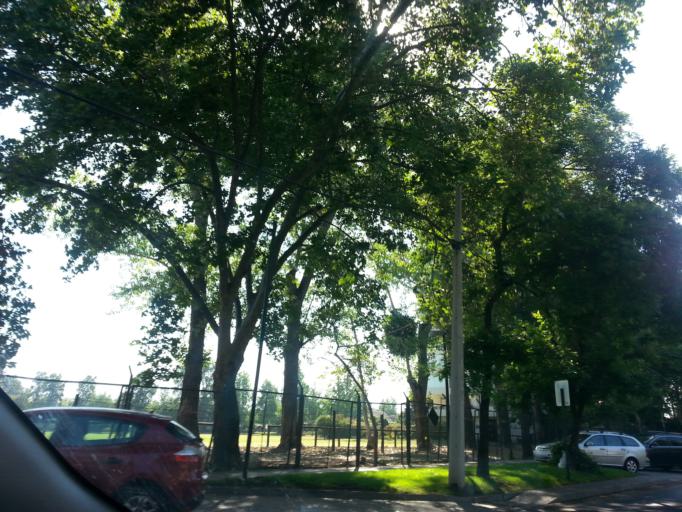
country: CL
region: Santiago Metropolitan
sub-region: Provincia de Santiago
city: Villa Presidente Frei, Nunoa, Santiago, Chile
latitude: -33.3891
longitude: -70.5886
